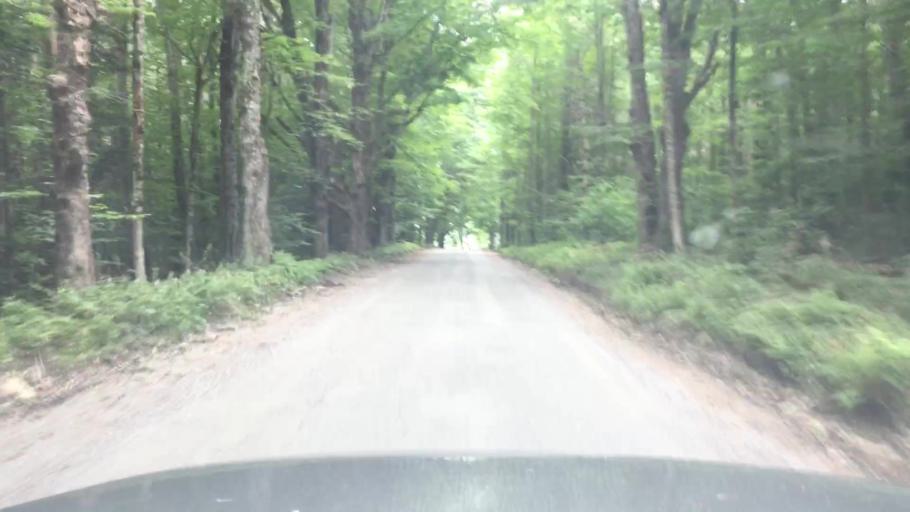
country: US
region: Vermont
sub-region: Windham County
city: Dover
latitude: 42.8245
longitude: -72.7619
